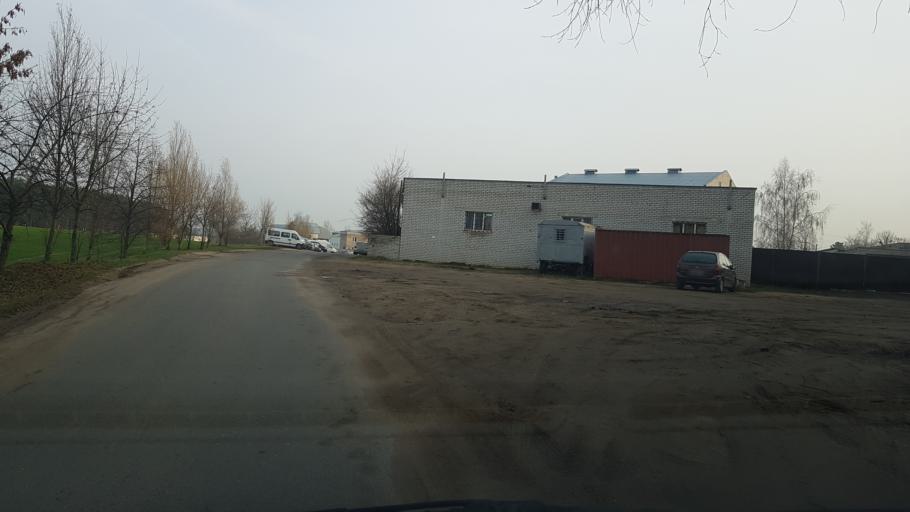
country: BY
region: Minsk
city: Bal'shavik
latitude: 53.9623
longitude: 27.5404
